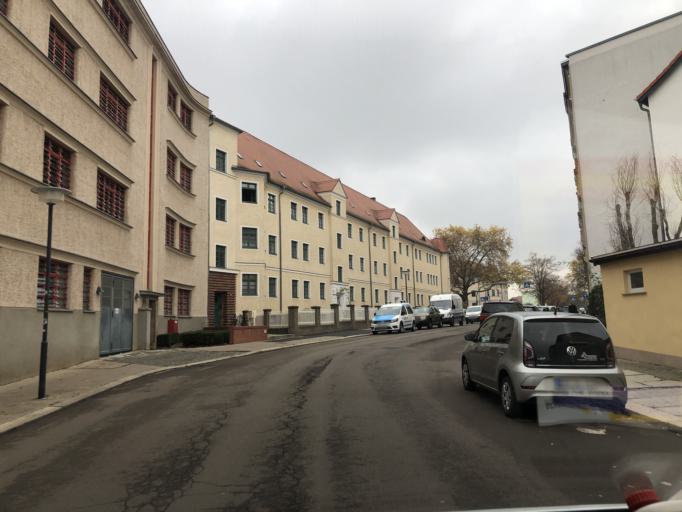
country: DE
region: Saxony-Anhalt
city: Halle (Saale)
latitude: 51.4711
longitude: 11.9731
